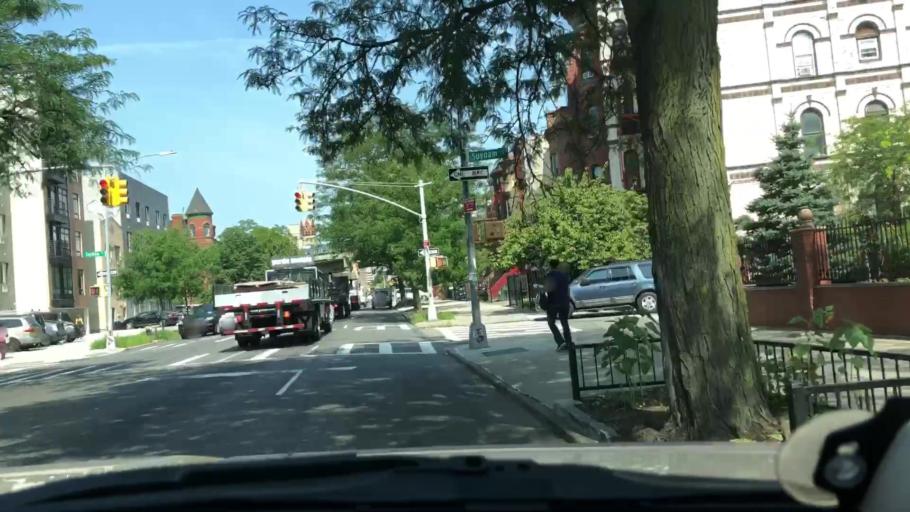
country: US
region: New York
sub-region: Kings County
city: Brooklyn
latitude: 40.6965
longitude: -73.9308
